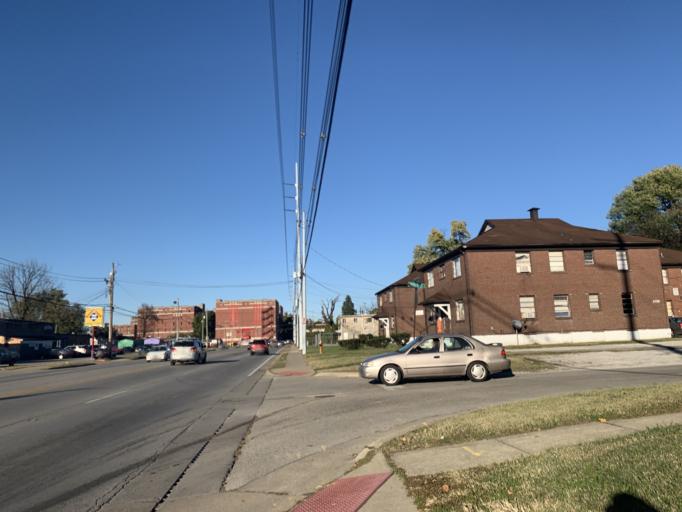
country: US
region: Kentucky
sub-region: Jefferson County
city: Shively
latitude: 38.2108
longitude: -85.7861
